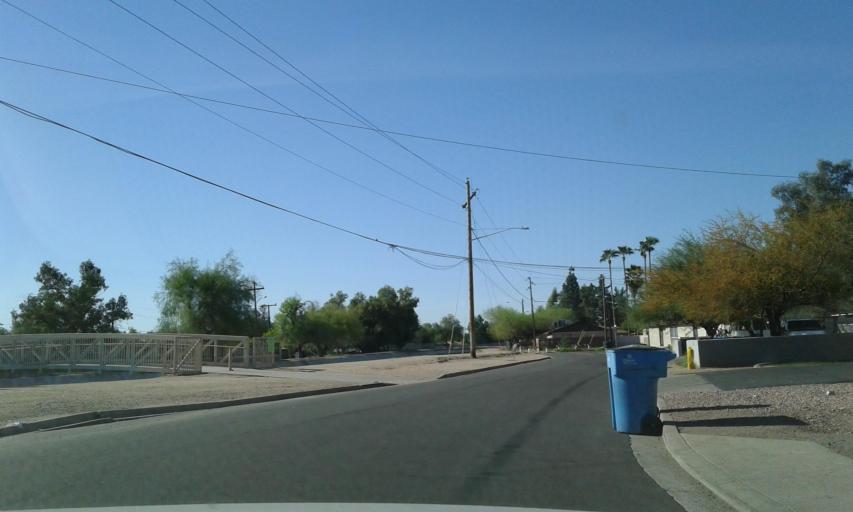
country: US
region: Arizona
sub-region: Maricopa County
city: Phoenix
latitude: 33.4941
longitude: -112.1084
